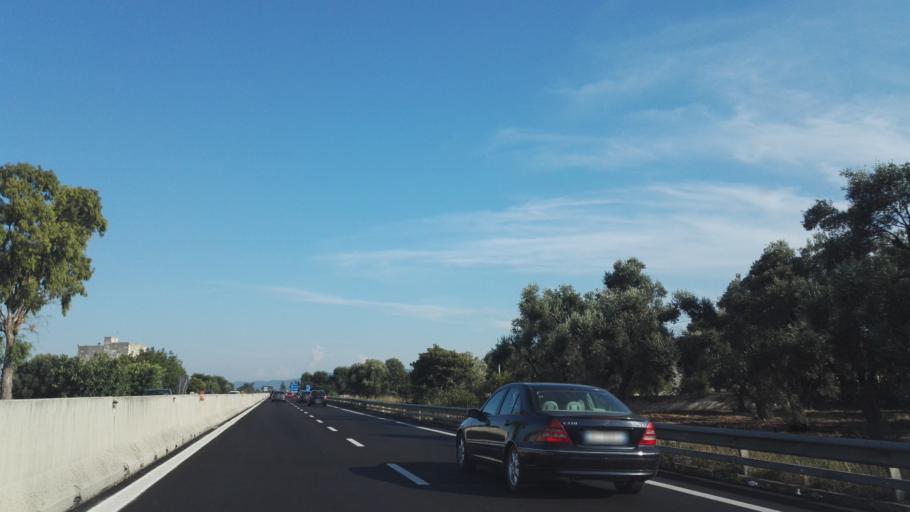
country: IT
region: Apulia
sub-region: Provincia di Brindisi
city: Fasano
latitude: 40.8472
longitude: 17.3616
